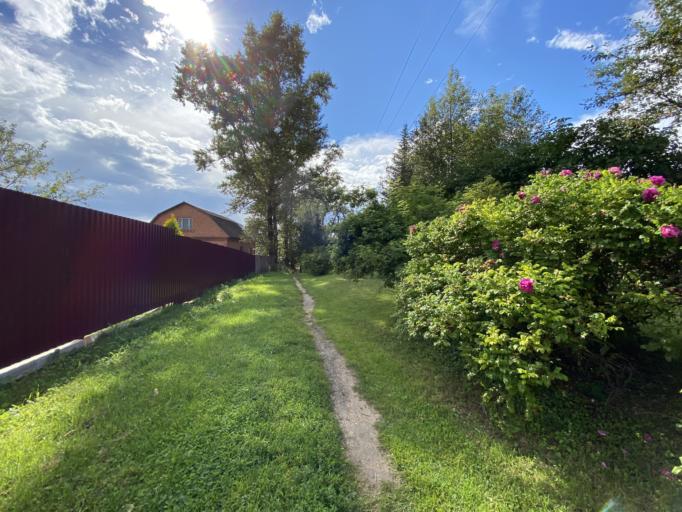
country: RU
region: Moskovskaya
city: Sergiyev Posad
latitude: 56.3081
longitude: 38.1588
